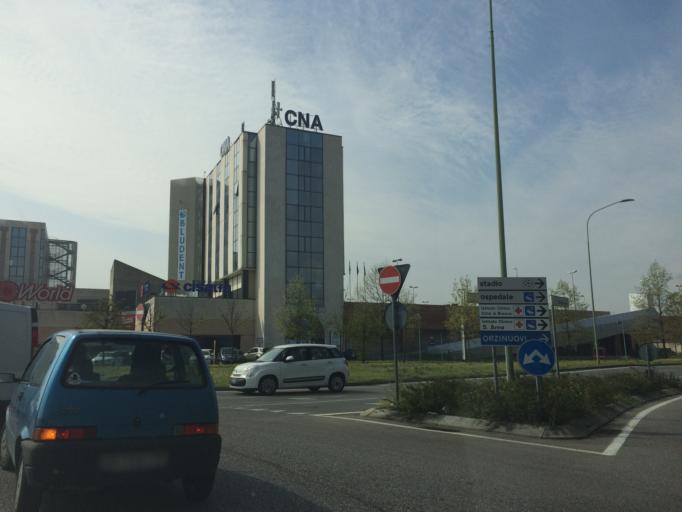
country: IT
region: Lombardy
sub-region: Provincia di Brescia
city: Brescia
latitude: 45.5272
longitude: 10.1979
